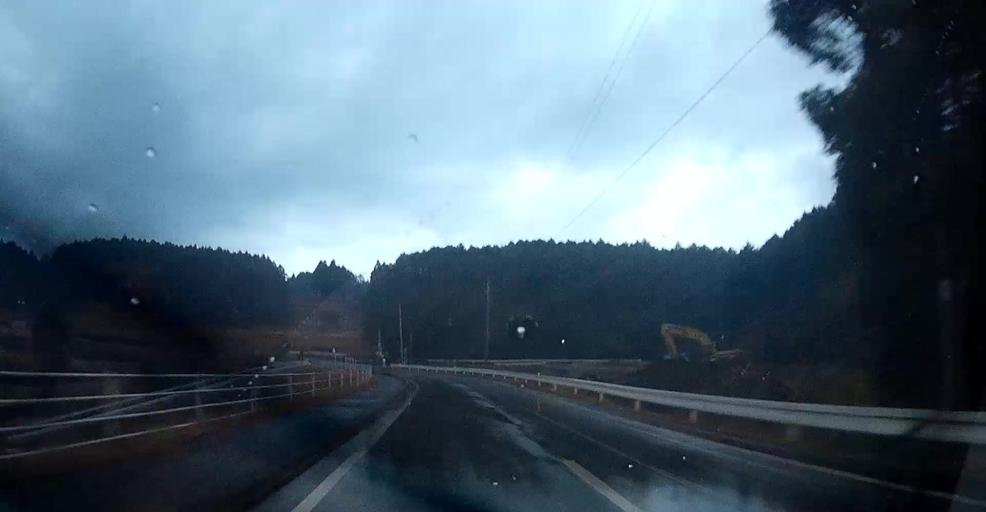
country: JP
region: Kumamoto
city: Ozu
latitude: 32.8261
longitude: 130.9148
